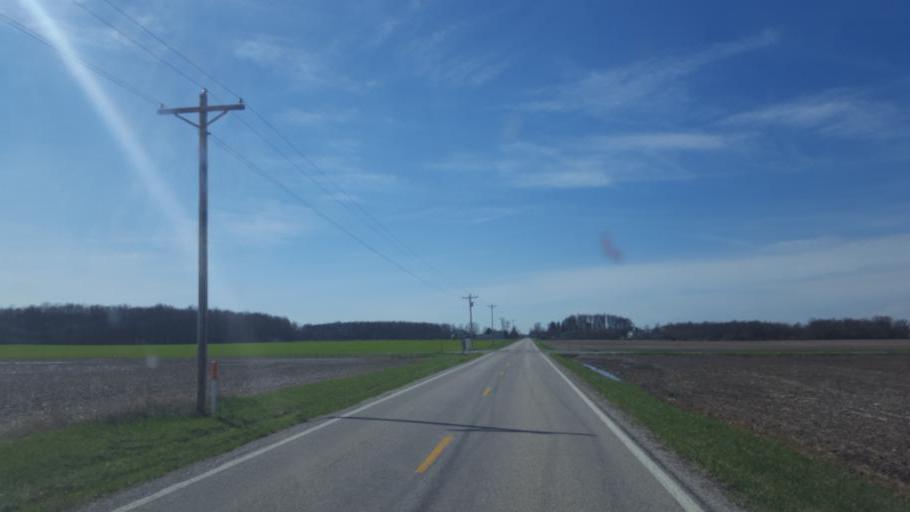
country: US
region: Ohio
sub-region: Morrow County
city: Cardington
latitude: 40.5152
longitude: -82.9628
